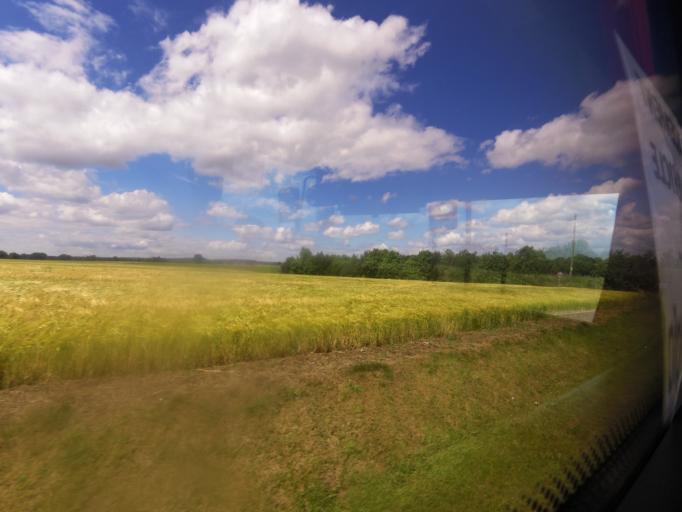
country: GB
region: England
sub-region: Norfolk
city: Aylsham
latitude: 52.7591
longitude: 1.2581
